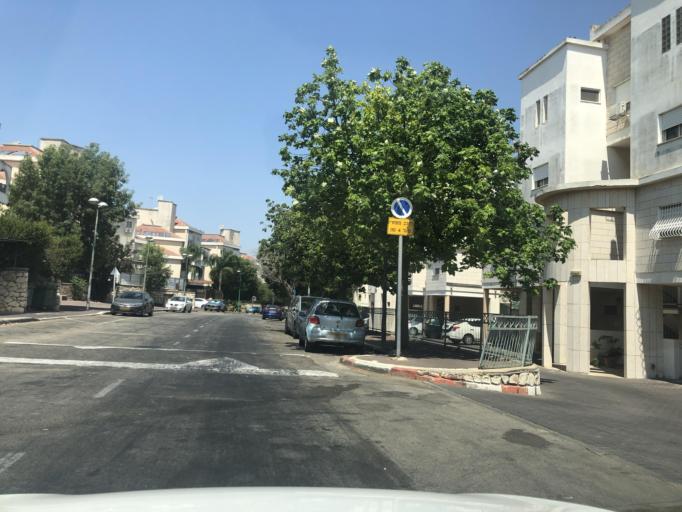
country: IL
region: Haifa
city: Daliyat el Karmil
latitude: 32.6375
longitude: 35.0895
